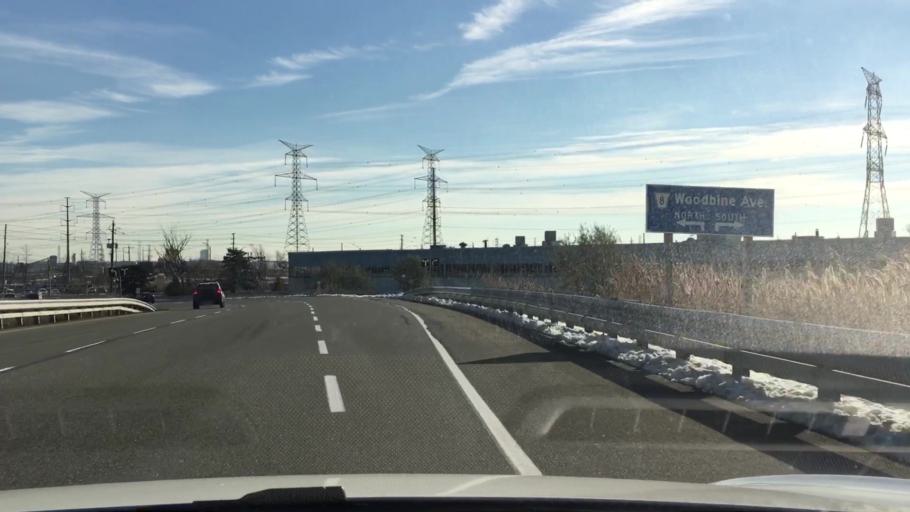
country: CA
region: Ontario
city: Willowdale
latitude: 43.8395
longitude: -79.3577
